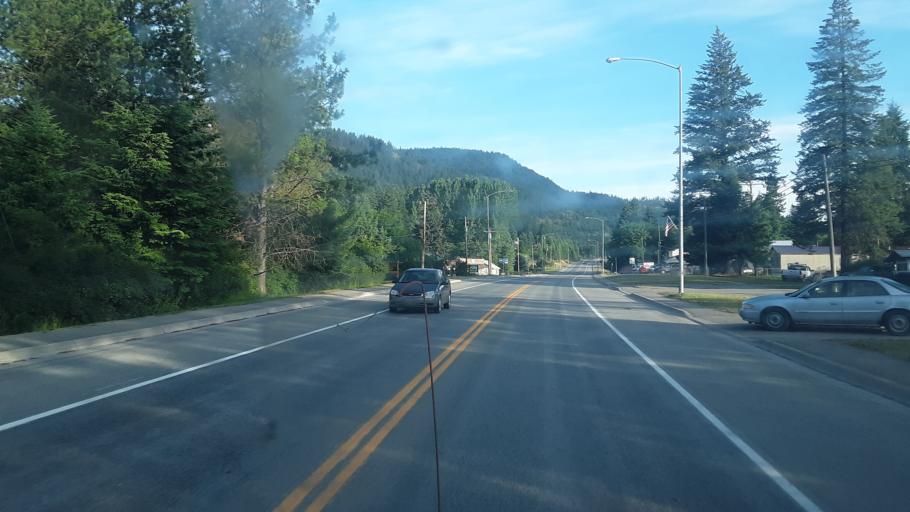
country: US
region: Montana
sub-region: Lincoln County
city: Libby
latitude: 48.4519
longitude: -115.8849
